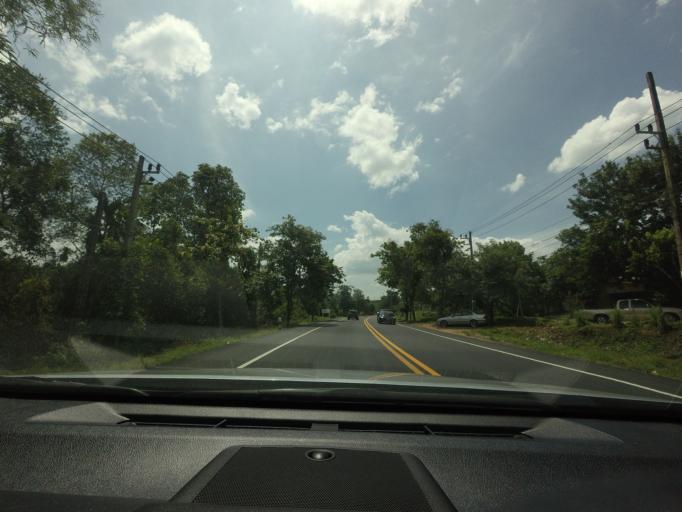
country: TH
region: Yala
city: Krong Pi Nang
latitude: 6.4682
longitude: 101.3271
